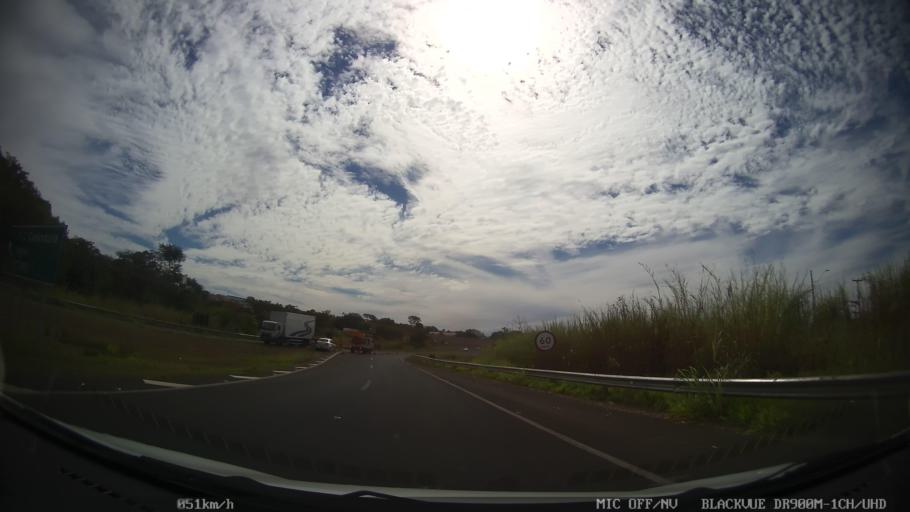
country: BR
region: Sao Paulo
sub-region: Catanduva
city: Catanduva
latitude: -21.1635
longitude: -48.9876
